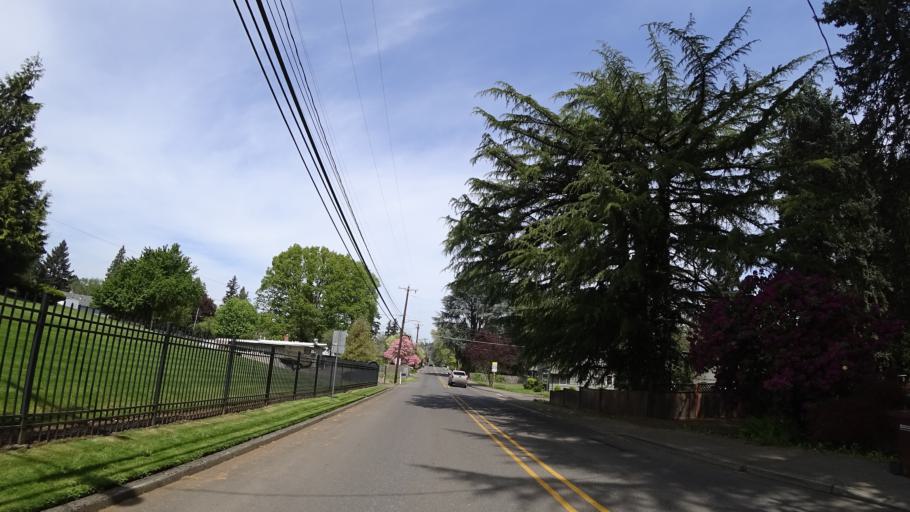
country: US
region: Oregon
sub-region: Clackamas County
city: Milwaukie
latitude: 45.4493
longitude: -122.6046
